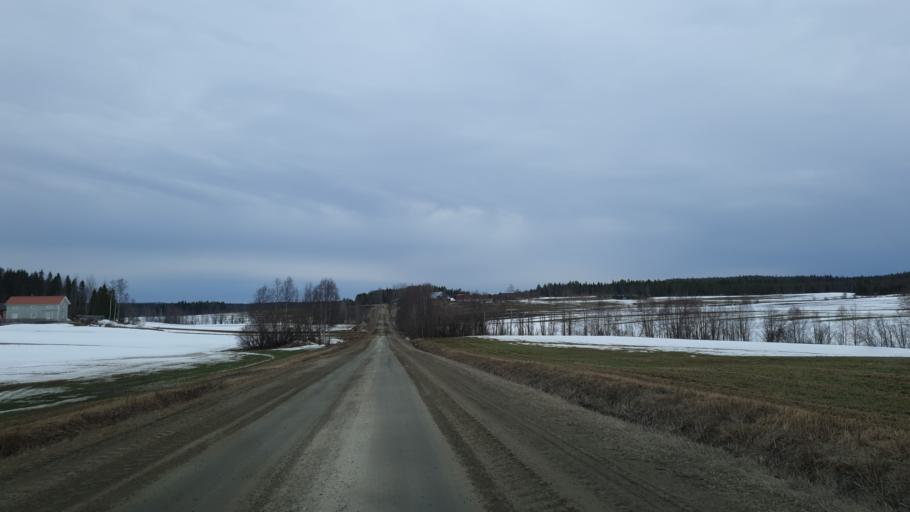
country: SE
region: Vaesterbotten
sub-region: Skelleftea Kommun
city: Burea
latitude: 64.3359
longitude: 21.1311
